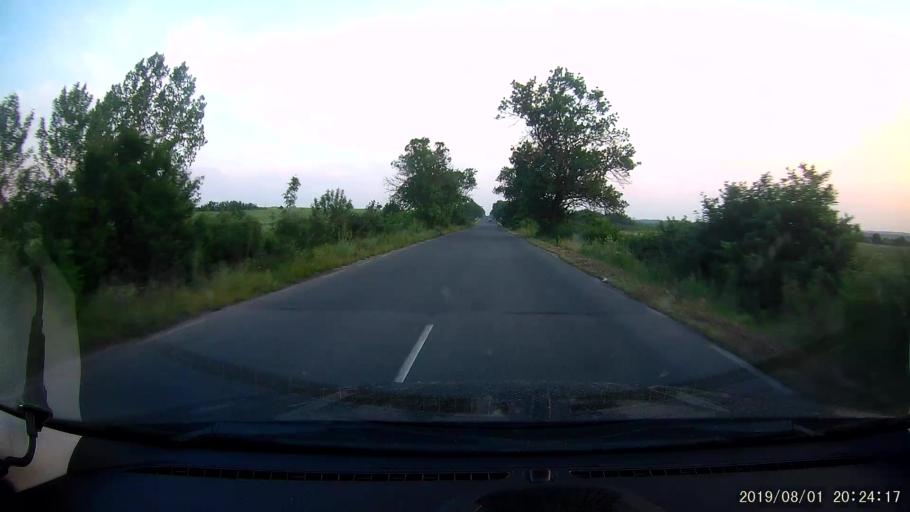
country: BG
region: Yambol
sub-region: Obshtina Elkhovo
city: Elkhovo
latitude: 42.2343
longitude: 26.5946
